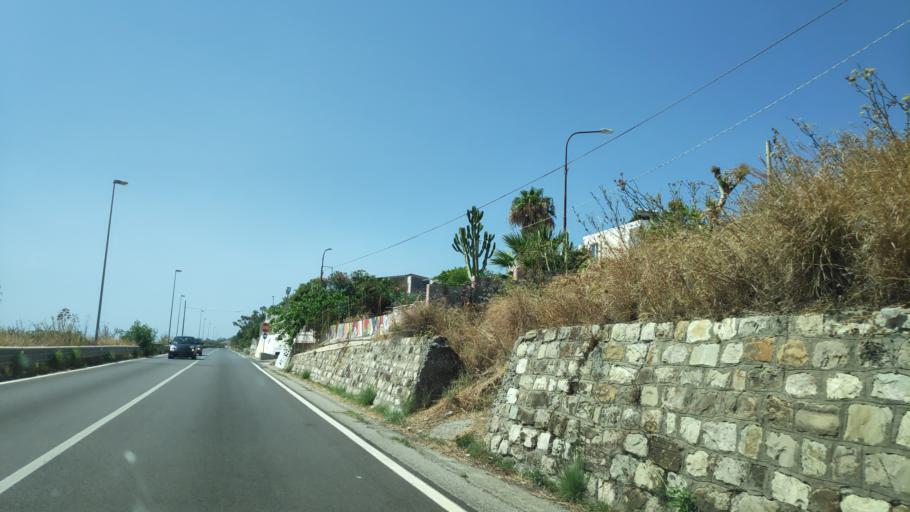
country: IT
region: Calabria
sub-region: Provincia di Reggio Calabria
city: Africo Nuovo
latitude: 38.0147
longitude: 16.1329
